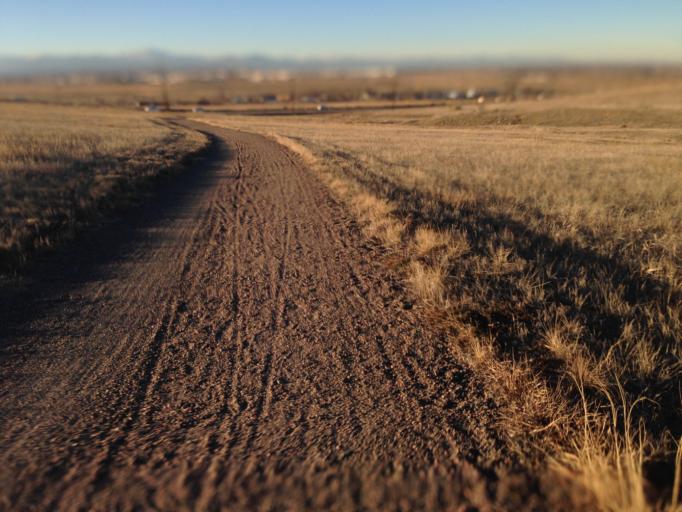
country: US
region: Colorado
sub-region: Broomfield County
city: Broomfield
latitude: 39.9444
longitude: -105.0880
